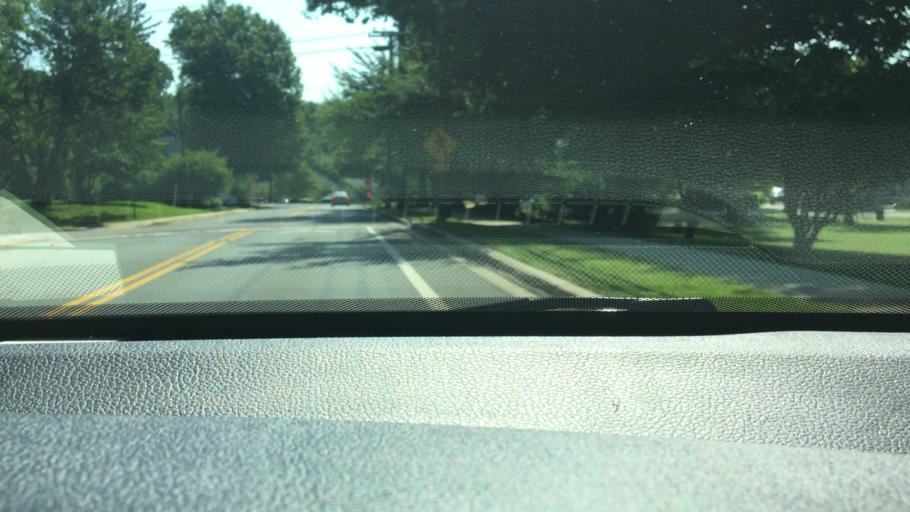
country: US
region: Maryland
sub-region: Montgomery County
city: North Kensington
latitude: 39.0298
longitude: -77.0719
